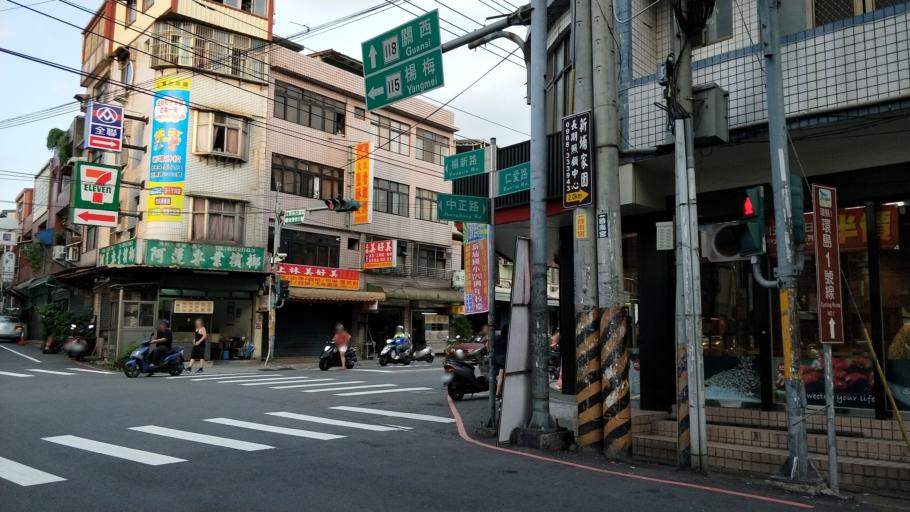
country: TW
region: Taiwan
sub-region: Hsinchu
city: Zhubei
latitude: 24.8273
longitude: 121.0810
